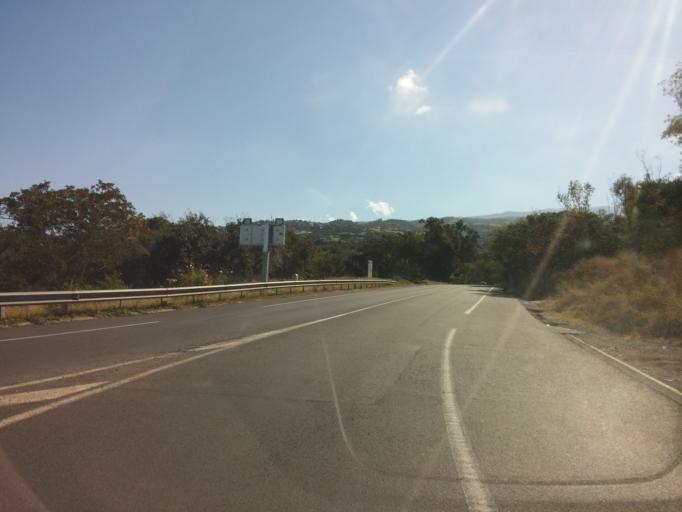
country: RE
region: Reunion
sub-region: Reunion
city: Les Avirons
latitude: -21.2625
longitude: 55.3391
